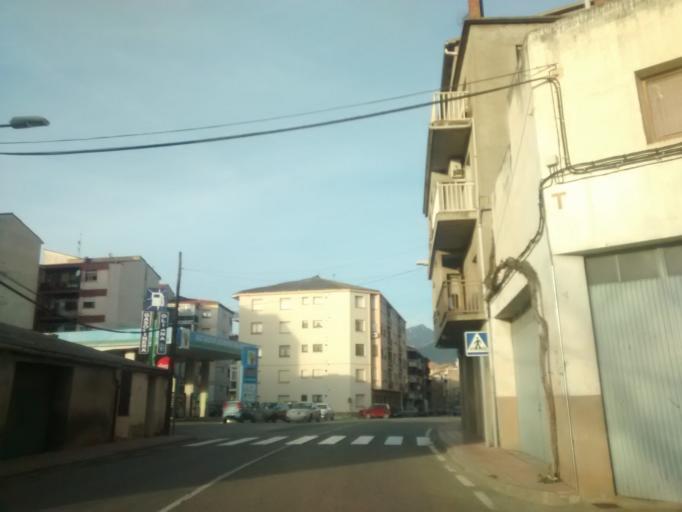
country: ES
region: Catalonia
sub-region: Provincia de Lleida
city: Oliana
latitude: 42.0639
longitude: 1.3129
